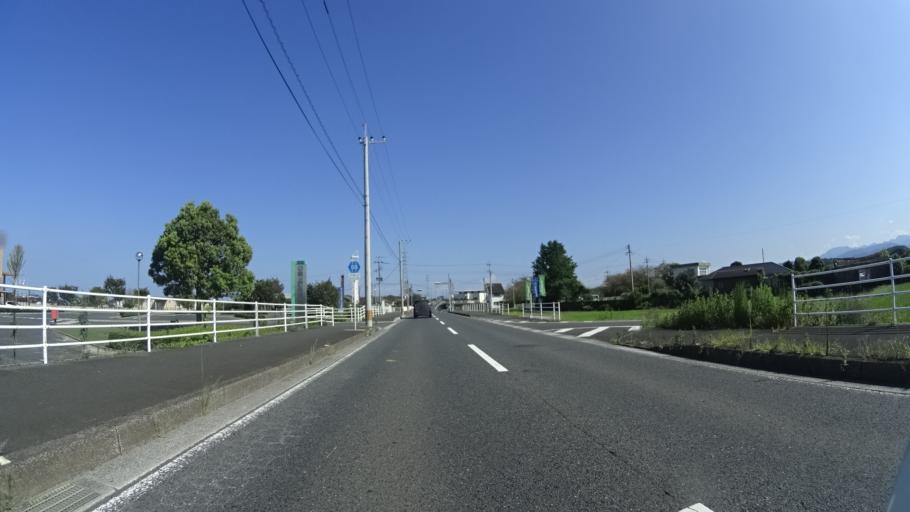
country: JP
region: Fukuoka
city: Tsuiki
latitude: 33.6646
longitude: 131.0293
